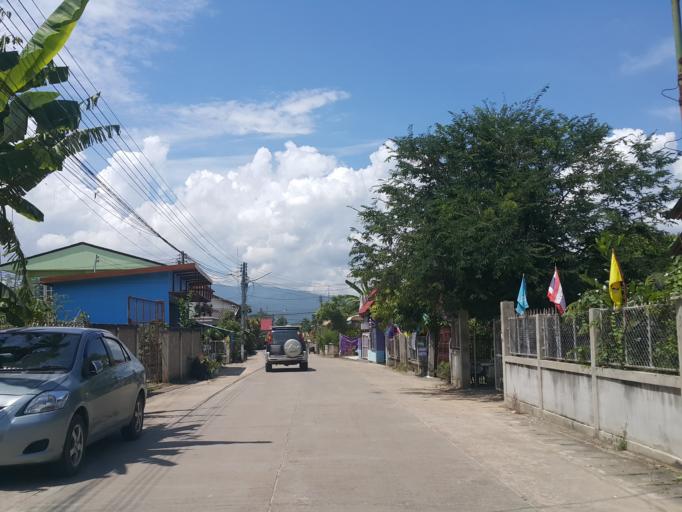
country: TH
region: Chiang Mai
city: Phrao
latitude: 19.3675
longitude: 99.2038
